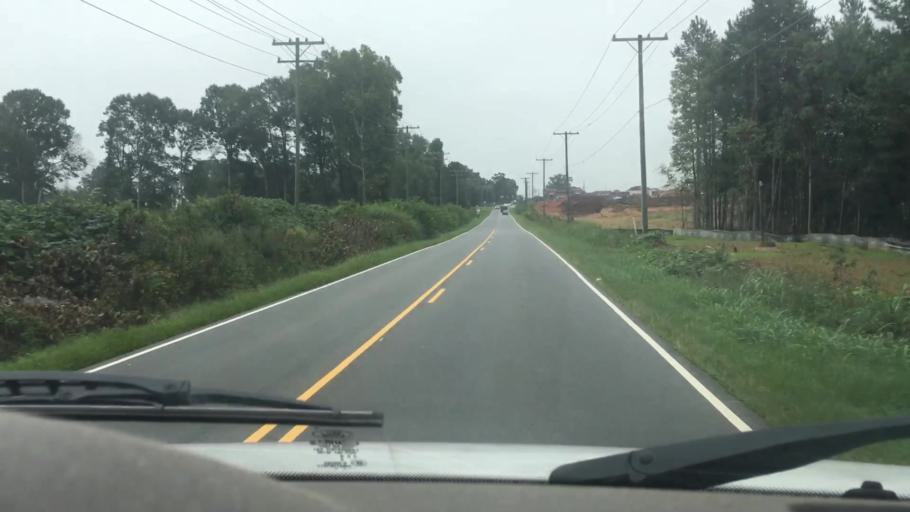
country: US
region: North Carolina
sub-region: Mecklenburg County
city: Huntersville
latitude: 35.4150
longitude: -80.7508
